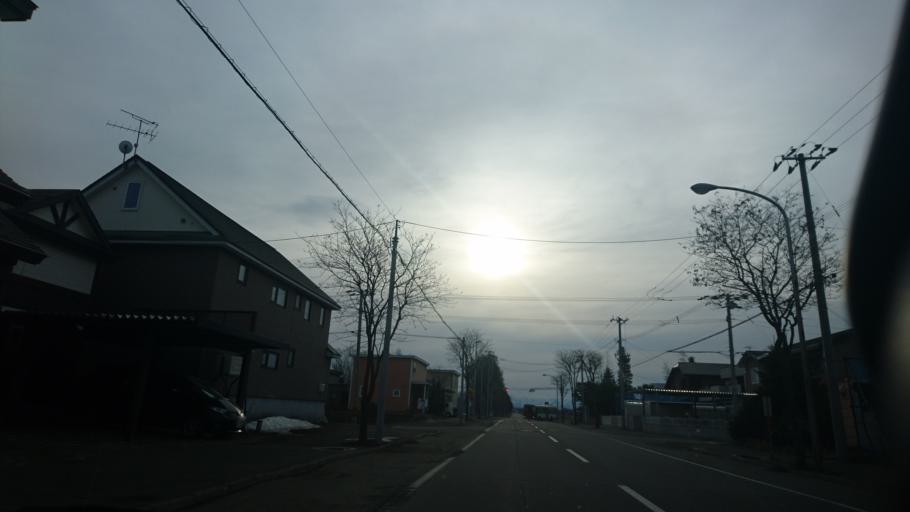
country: JP
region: Hokkaido
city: Otofuke
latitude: 43.0014
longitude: 143.1894
